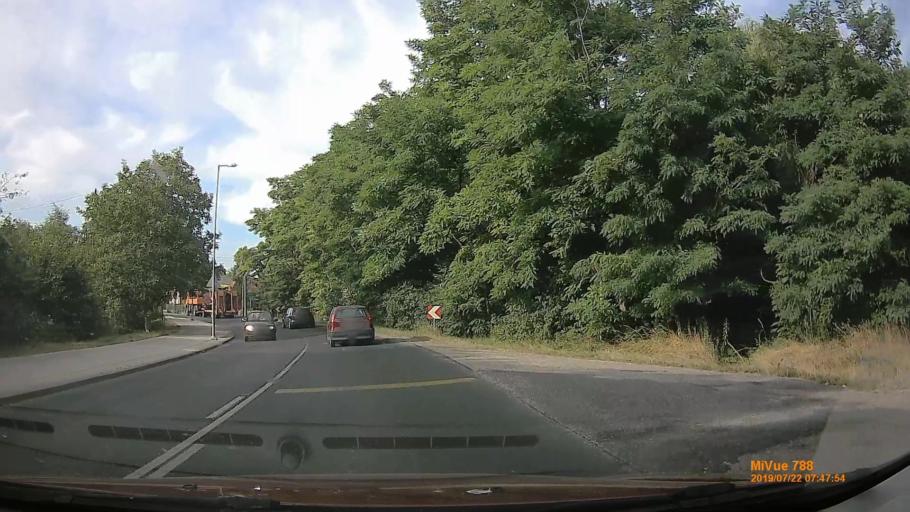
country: HU
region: Veszprem
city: Ajka
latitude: 47.0780
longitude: 17.5469
